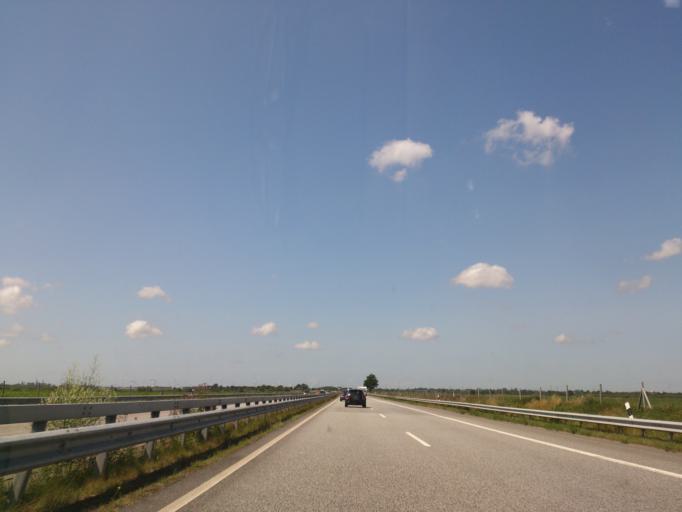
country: DE
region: Schleswig-Holstein
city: Nordhastedt
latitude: 54.1653
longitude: 9.1509
